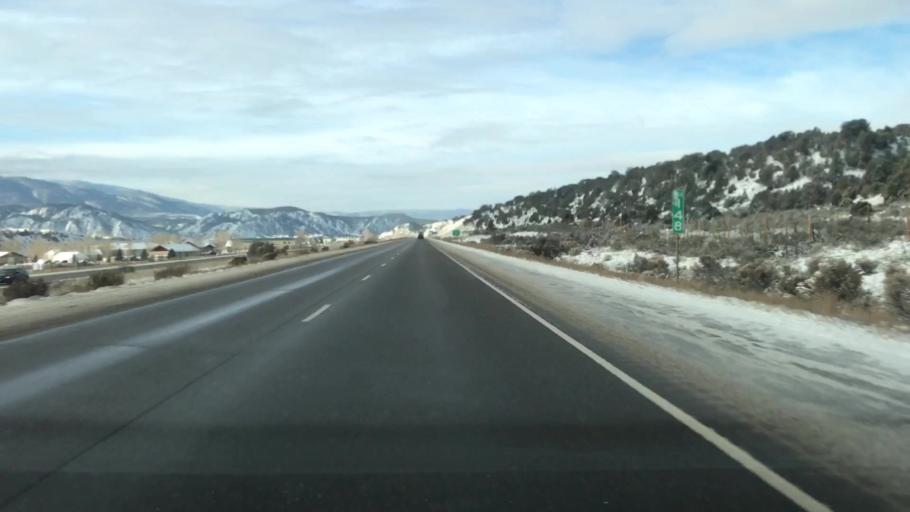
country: US
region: Colorado
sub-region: Eagle County
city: Eagle
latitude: 39.6703
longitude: -106.8057
